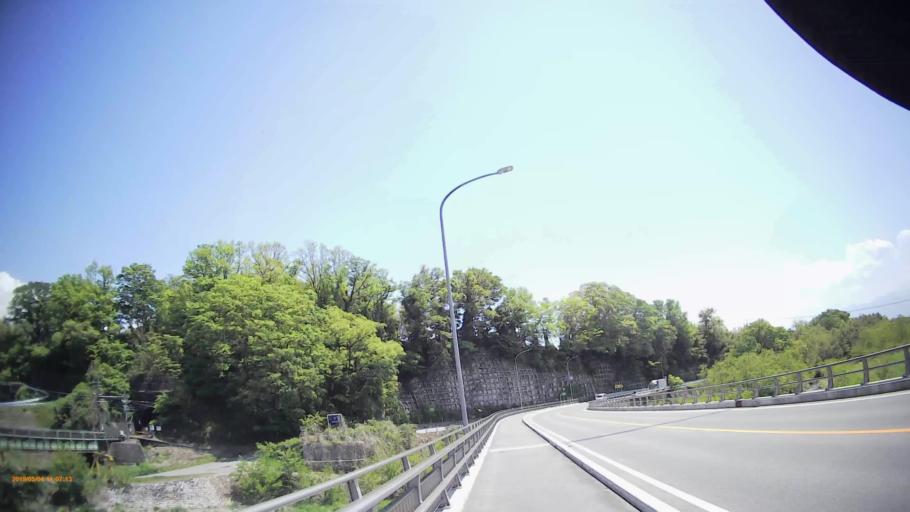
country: JP
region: Yamanashi
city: Nirasaki
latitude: 35.6976
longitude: 138.4679
